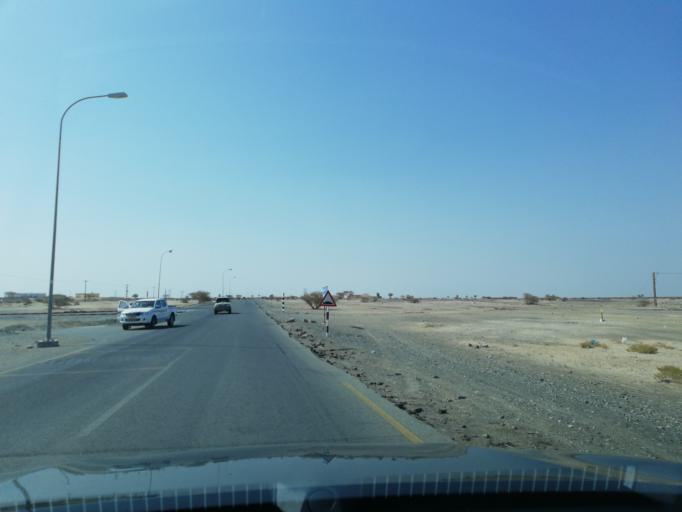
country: OM
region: Muhafazat ad Dakhiliyah
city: Adam
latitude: 22.3653
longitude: 58.0625
